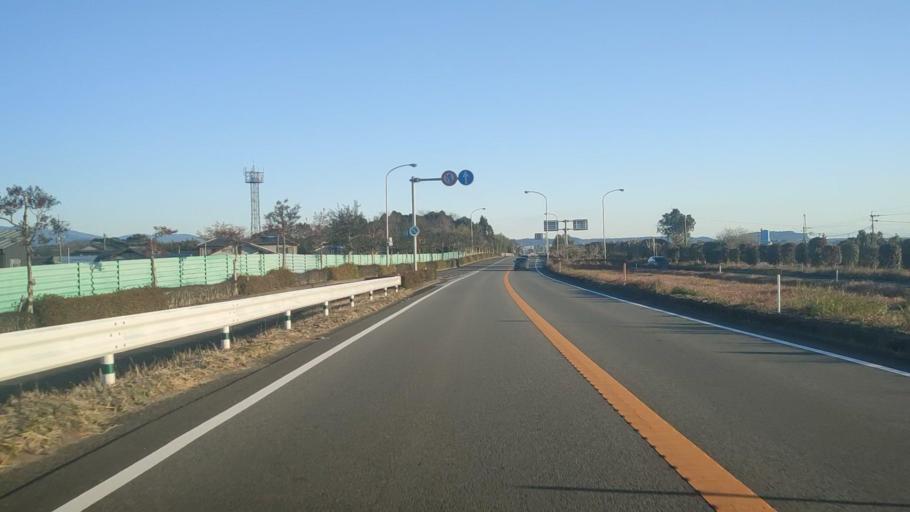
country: JP
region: Miyazaki
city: Tsuma
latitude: 32.0367
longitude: 131.4665
